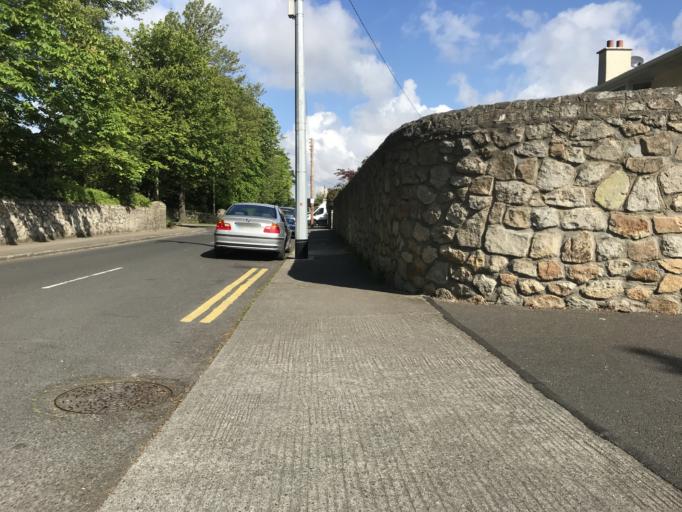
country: IE
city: Booterstown
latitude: 53.2993
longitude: -6.2001
